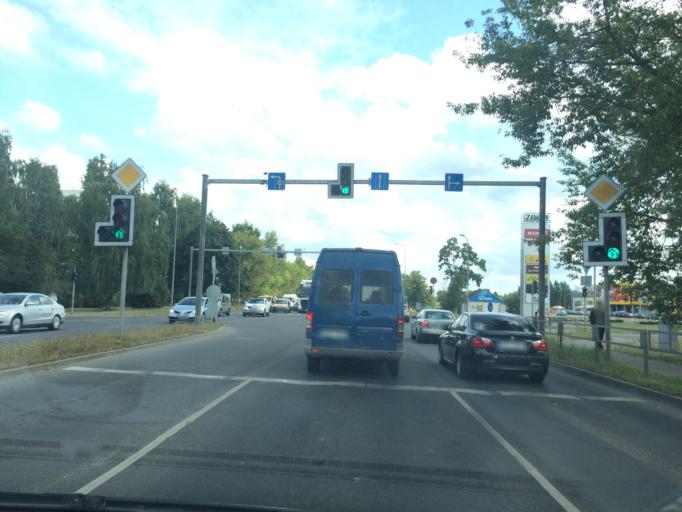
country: LV
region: Kekava
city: Kekava
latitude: 56.9001
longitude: 24.2030
